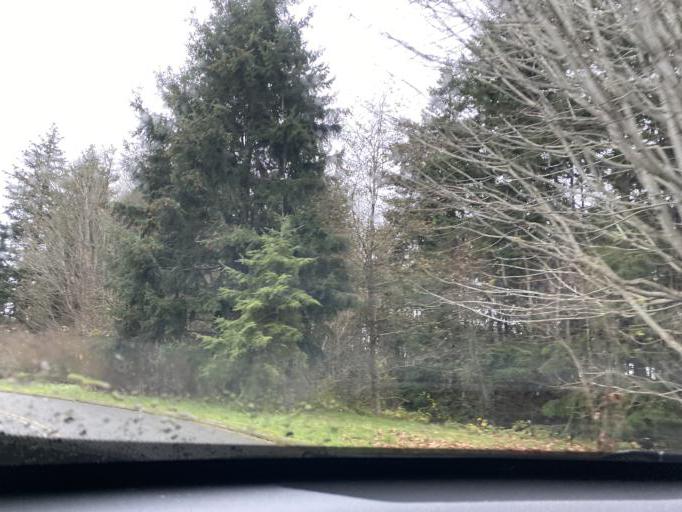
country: US
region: Washington
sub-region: King County
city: Seattle
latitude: 47.6619
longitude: -122.4210
